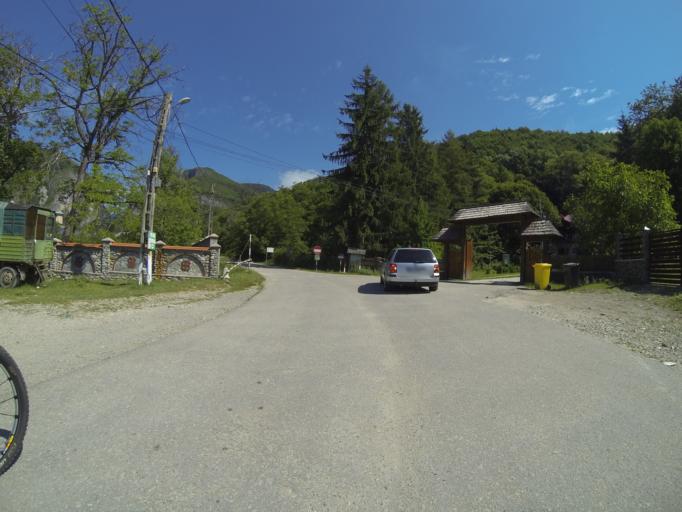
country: RO
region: Gorj
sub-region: Comuna Polovragi
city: Polovragi
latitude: 45.1913
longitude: 23.7909
